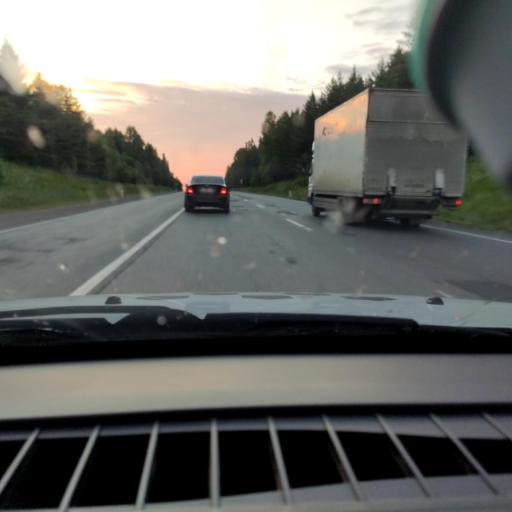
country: RU
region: Perm
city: Kungur
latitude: 57.3183
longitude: 56.9677
